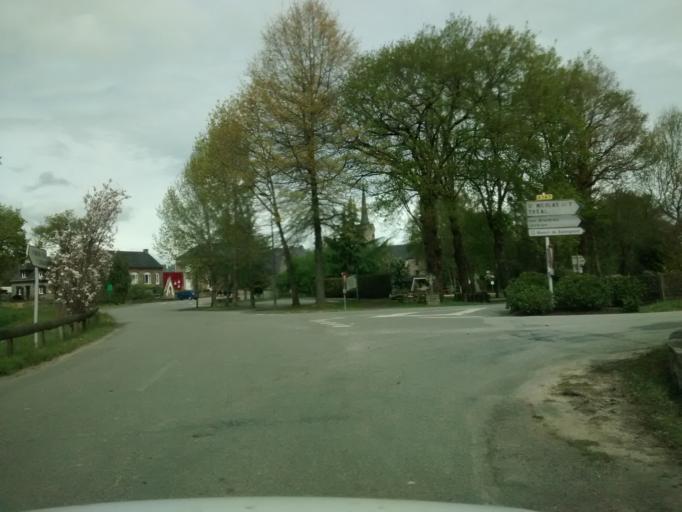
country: FR
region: Brittany
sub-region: Departement du Morbihan
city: Ruffiac
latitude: 47.7932
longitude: -2.3181
